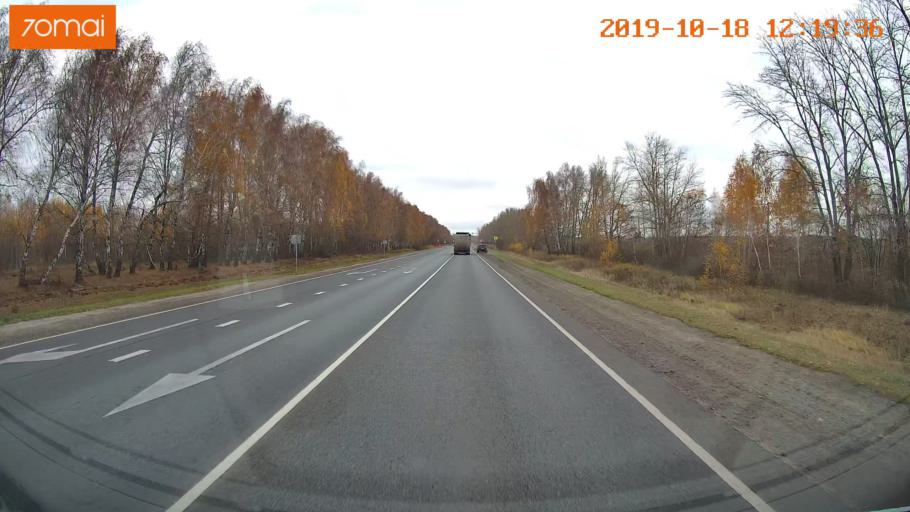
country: RU
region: Rjazan
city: Zakharovo
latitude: 54.4850
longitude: 39.4702
